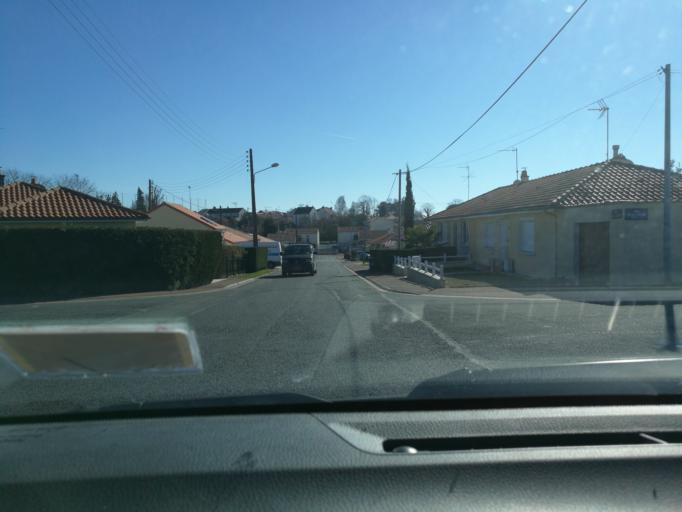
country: FR
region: Centre
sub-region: Departement du Loiret
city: Saint-Jean-de-la-Ruelle
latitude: 47.9007
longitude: 1.8659
